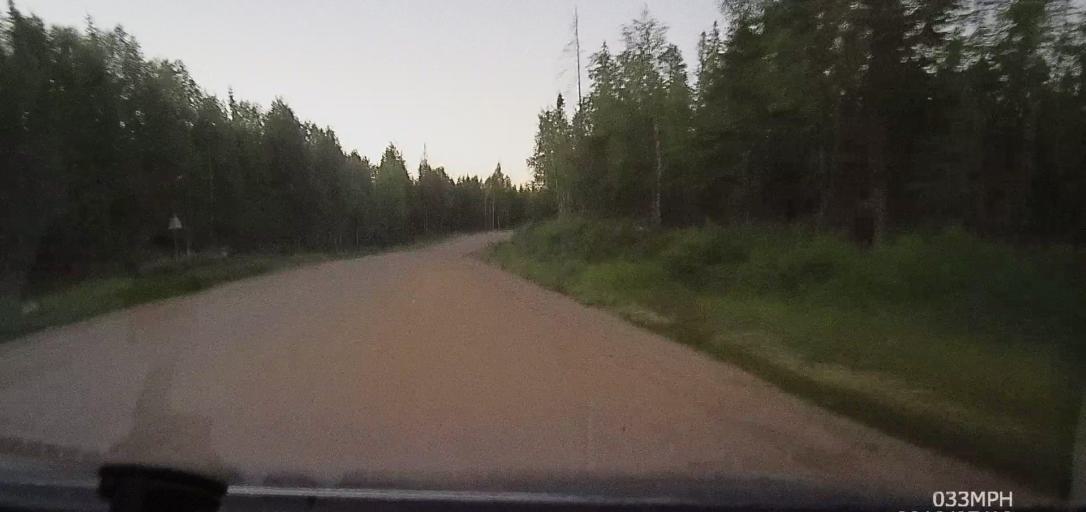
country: RU
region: Arkhangelskaya
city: Pinega
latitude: 64.4317
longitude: 43.1274
